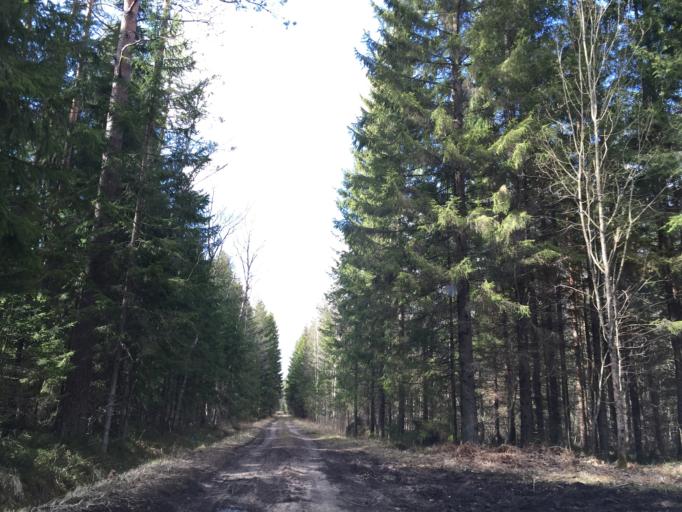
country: LV
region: Garkalne
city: Garkalne
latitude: 56.9494
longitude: 24.4769
